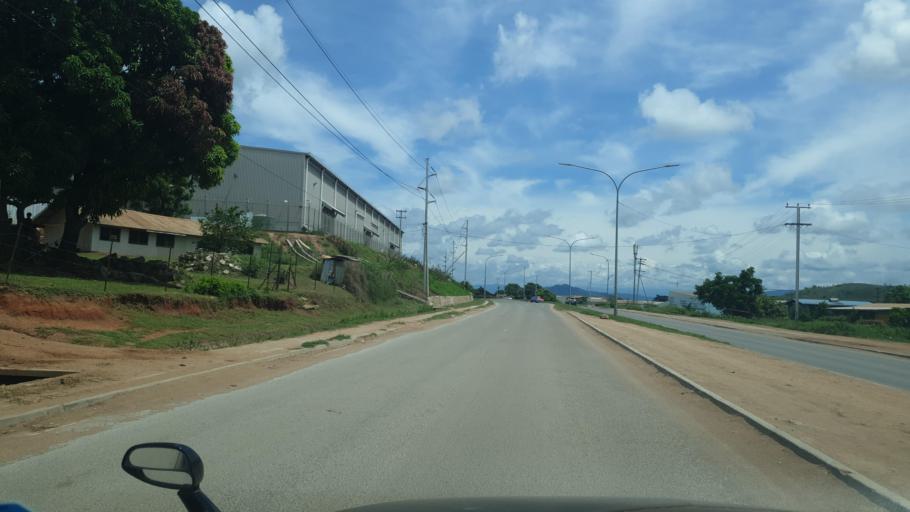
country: PG
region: National Capital
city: Port Moresby
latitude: -9.3885
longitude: 147.1537
